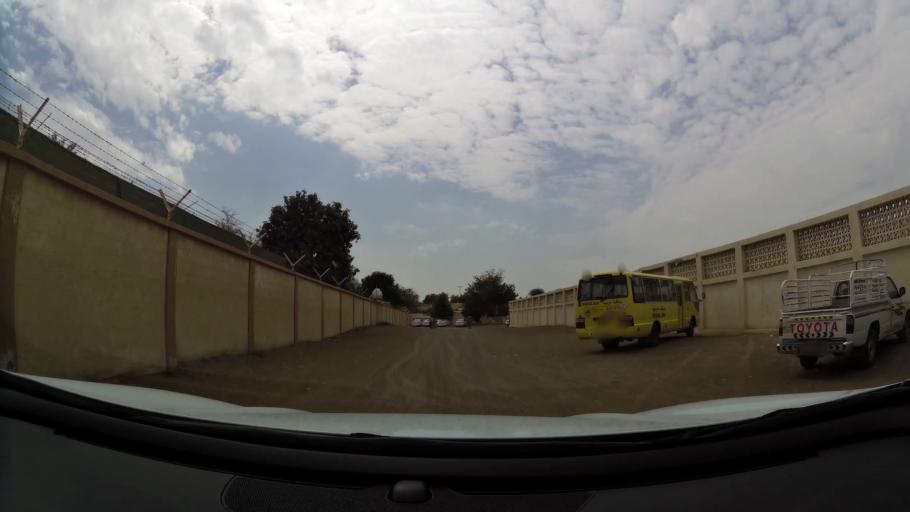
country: OM
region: Al Buraimi
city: Al Buraymi
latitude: 24.2174
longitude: 55.7875
